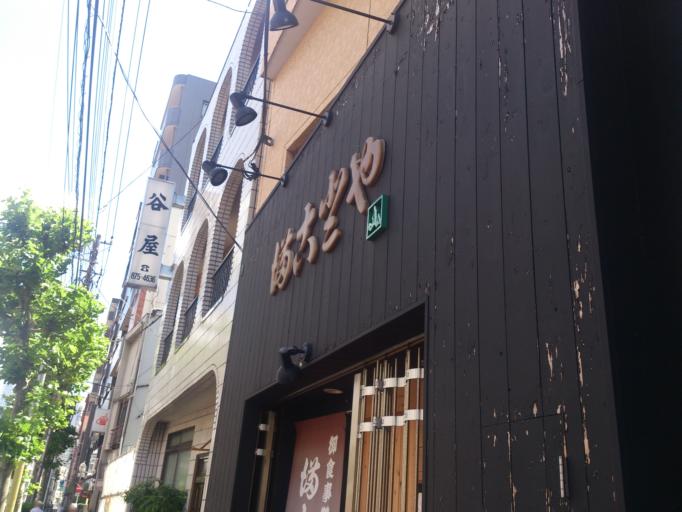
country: JP
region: Saitama
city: Soka
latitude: 35.7268
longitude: 139.8004
